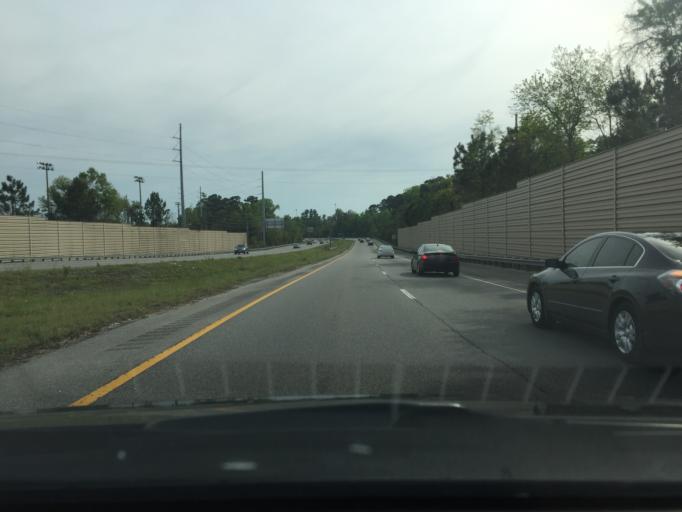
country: US
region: Georgia
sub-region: Chatham County
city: Isle of Hope
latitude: 31.9981
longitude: -81.0804
